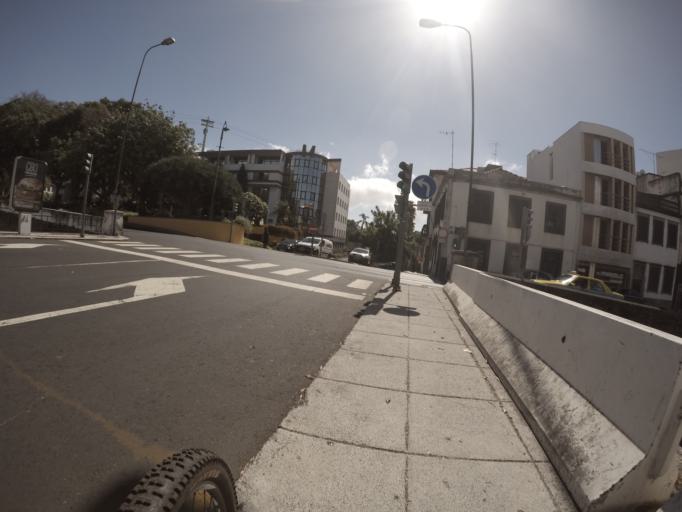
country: PT
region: Madeira
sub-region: Funchal
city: Nossa Senhora do Monte
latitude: 32.6504
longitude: -16.9032
